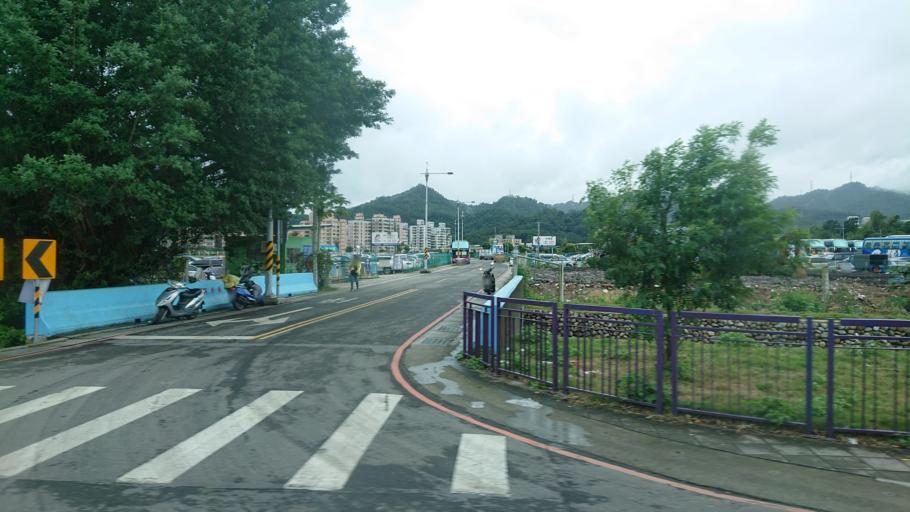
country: TW
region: Taipei
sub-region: Taipei
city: Banqiao
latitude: 24.9807
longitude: 121.4552
